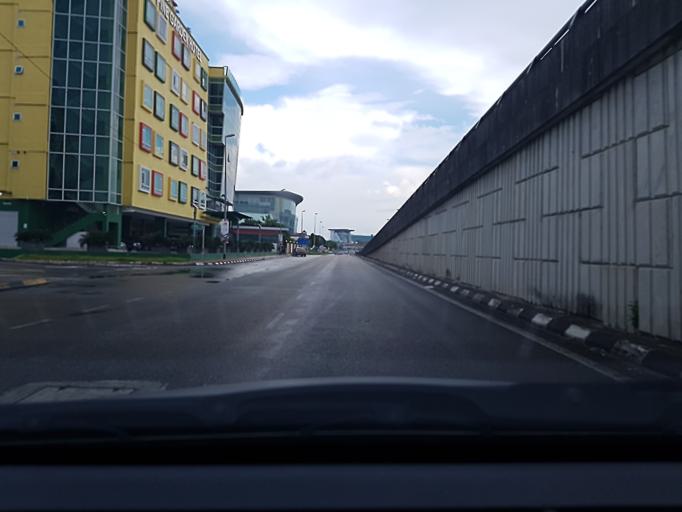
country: MY
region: Sarawak
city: Kuching
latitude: 1.5199
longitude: 110.3540
